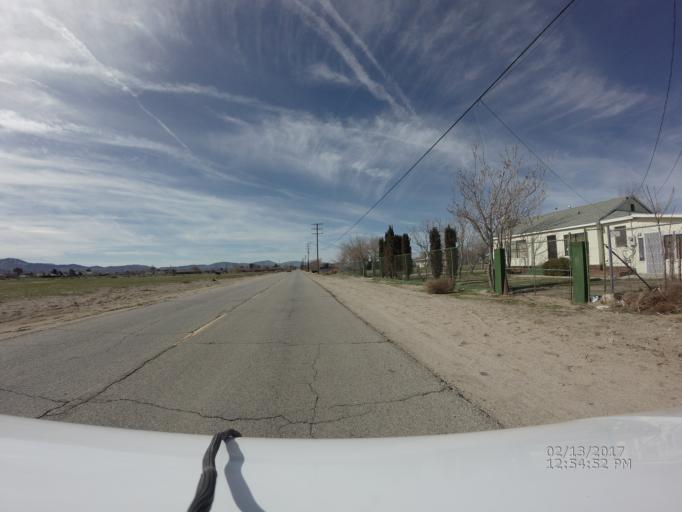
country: US
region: California
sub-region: Los Angeles County
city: Littlerock
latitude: 34.5724
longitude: -117.9578
